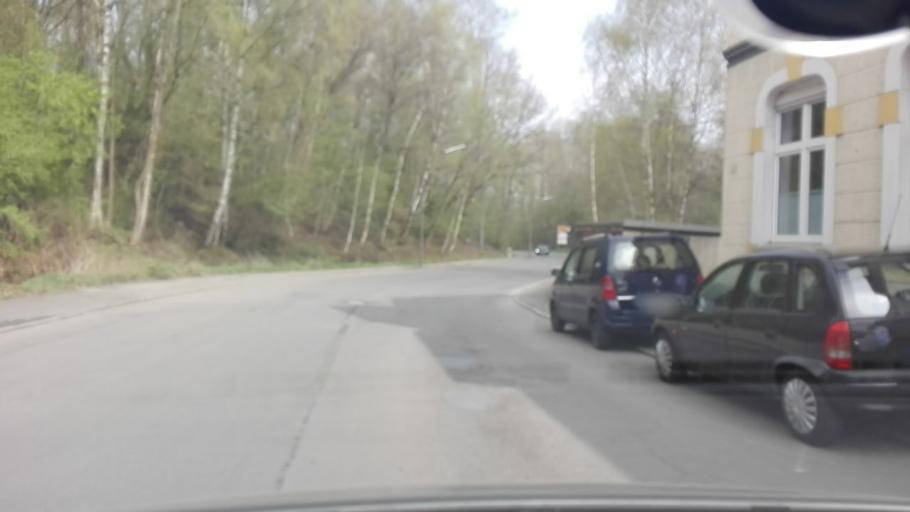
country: DE
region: North Rhine-Westphalia
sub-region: Regierungsbezirk Arnsberg
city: Dortmund
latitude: 51.4695
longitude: 7.4264
